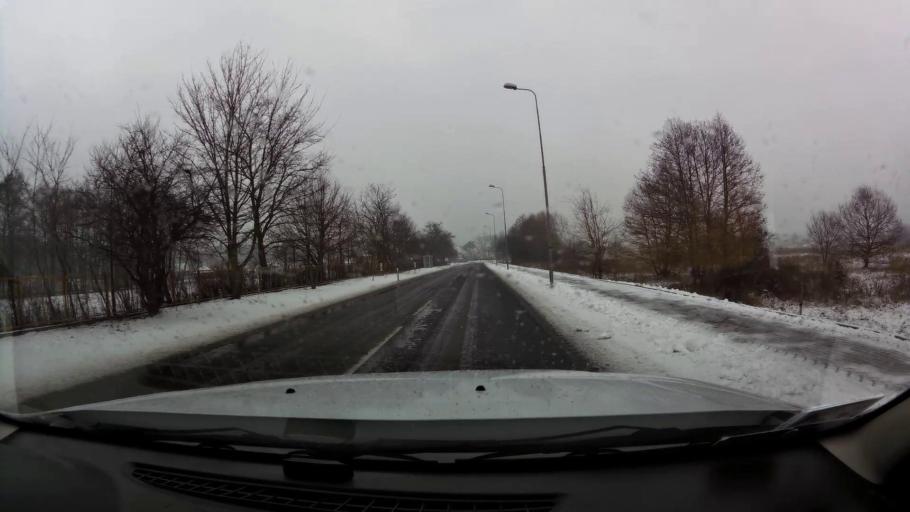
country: PL
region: West Pomeranian Voivodeship
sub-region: Powiat gryficki
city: Mrzezyno
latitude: 54.1395
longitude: 15.2868
